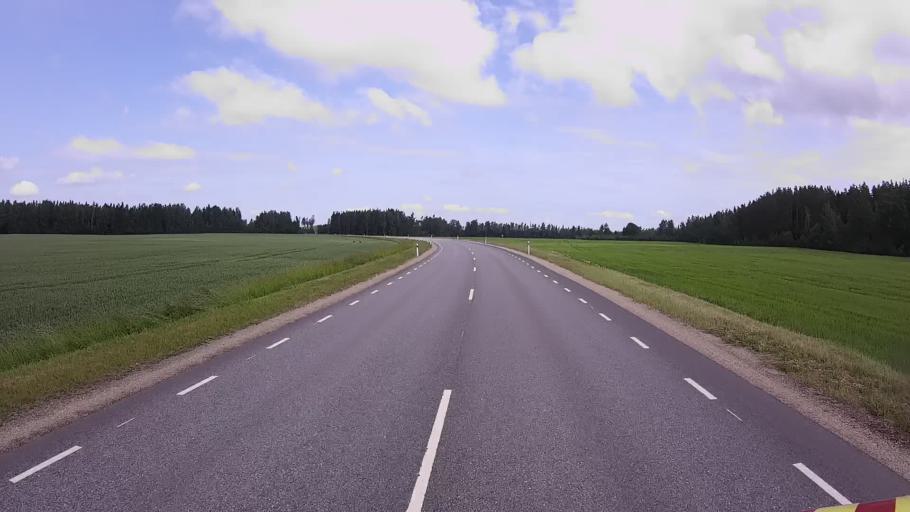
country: EE
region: Polvamaa
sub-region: Polva linn
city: Polva
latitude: 58.1283
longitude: 26.9561
